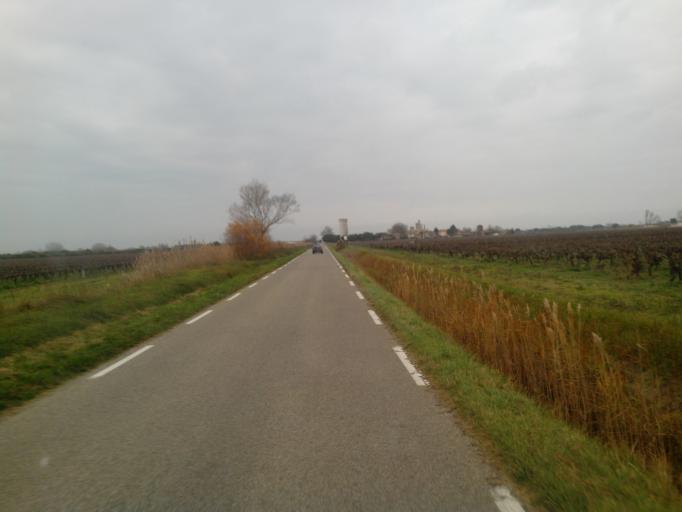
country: FR
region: Languedoc-Roussillon
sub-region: Departement du Gard
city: Aigues-Mortes
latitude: 43.5685
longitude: 4.3232
